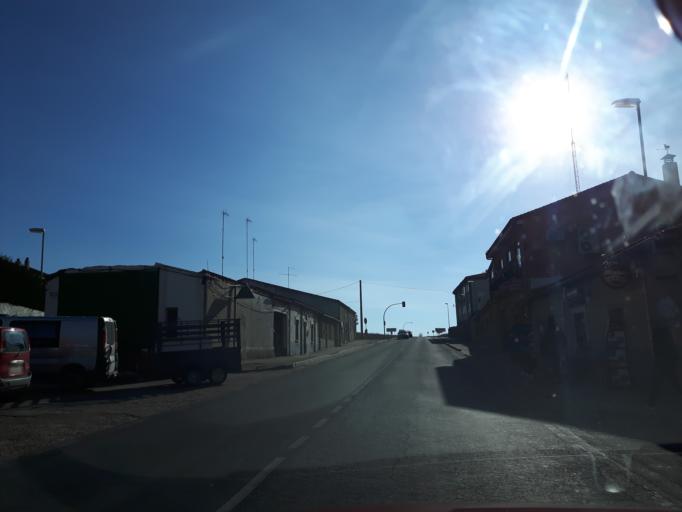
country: ES
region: Castille and Leon
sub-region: Provincia de Salamanca
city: San Cristobal de la Cuesta
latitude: 41.0281
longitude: -5.6189
